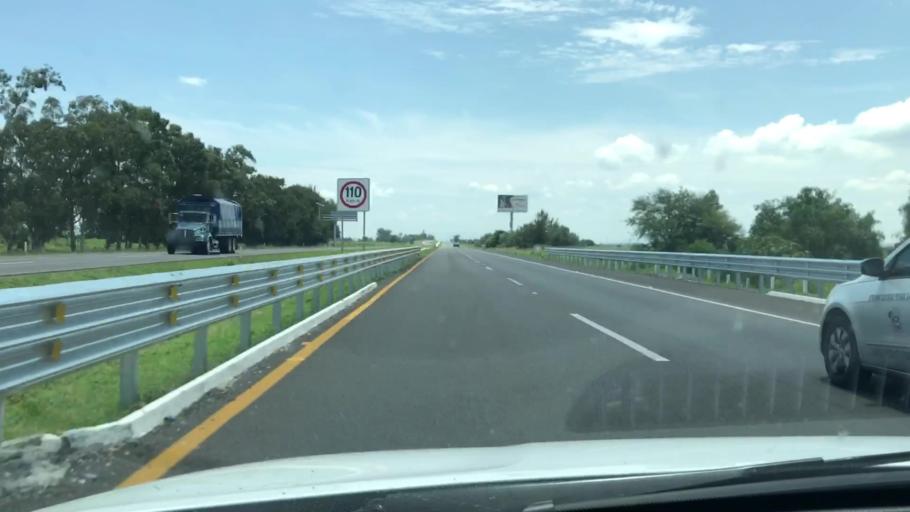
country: MX
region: Guanajuato
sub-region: Irapuato
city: Cuarta Brigada
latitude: 20.6496
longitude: -101.2812
